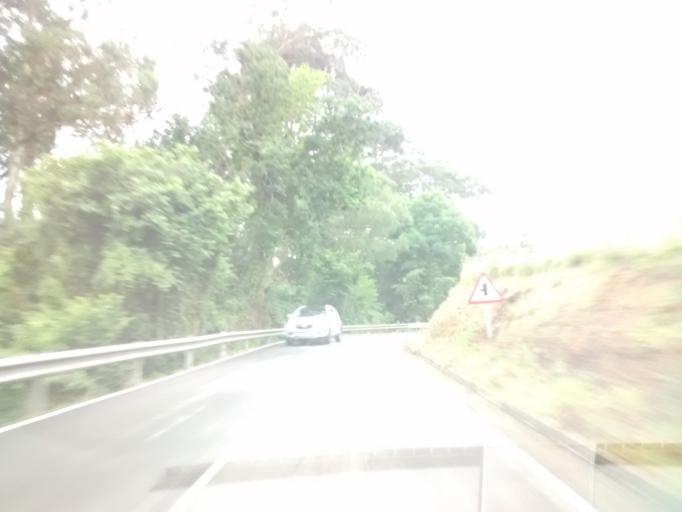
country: ES
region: Asturias
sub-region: Province of Asturias
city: Villaviciosa
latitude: 43.5358
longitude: -5.4150
